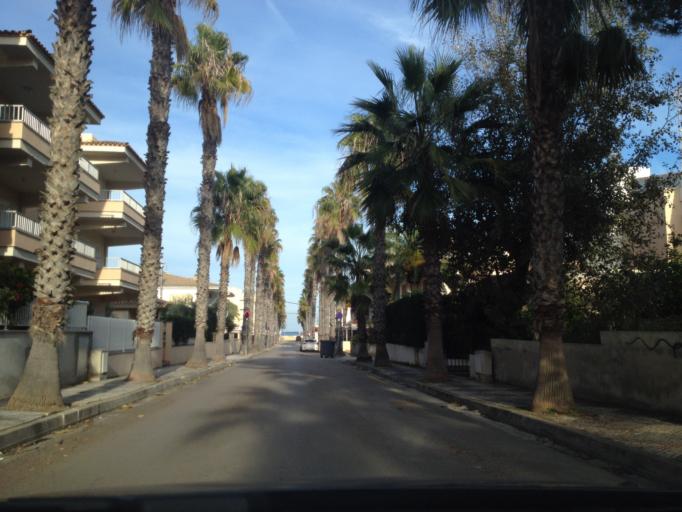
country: ES
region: Balearic Islands
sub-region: Illes Balears
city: Port d'Alcudia
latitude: 39.7687
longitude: 3.1472
